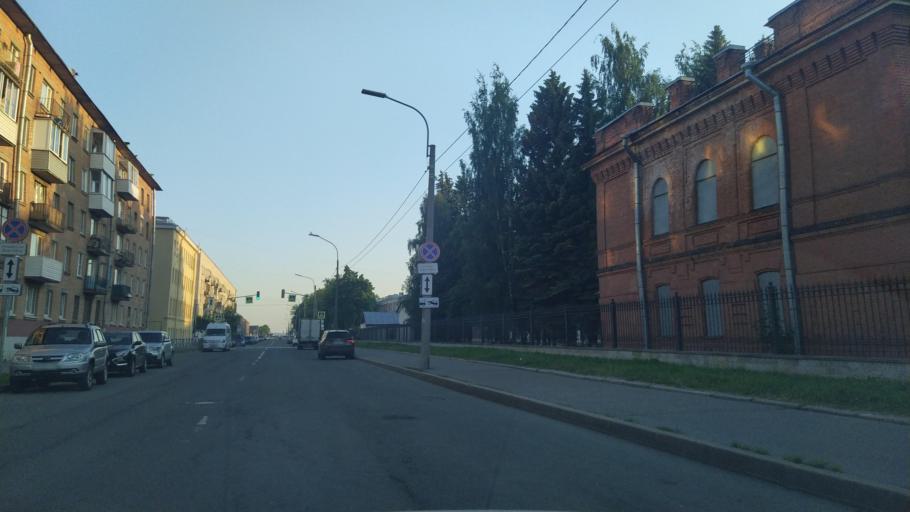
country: RU
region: St.-Petersburg
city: Kronshtadt
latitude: 59.9956
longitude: 29.7578
